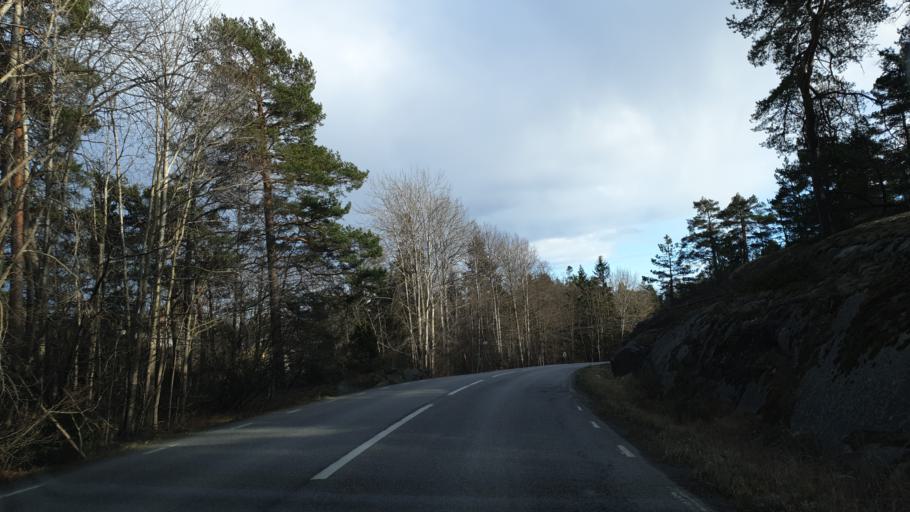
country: SE
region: Stockholm
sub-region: Varmdo Kommun
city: Holo
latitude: 59.3288
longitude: 18.7226
